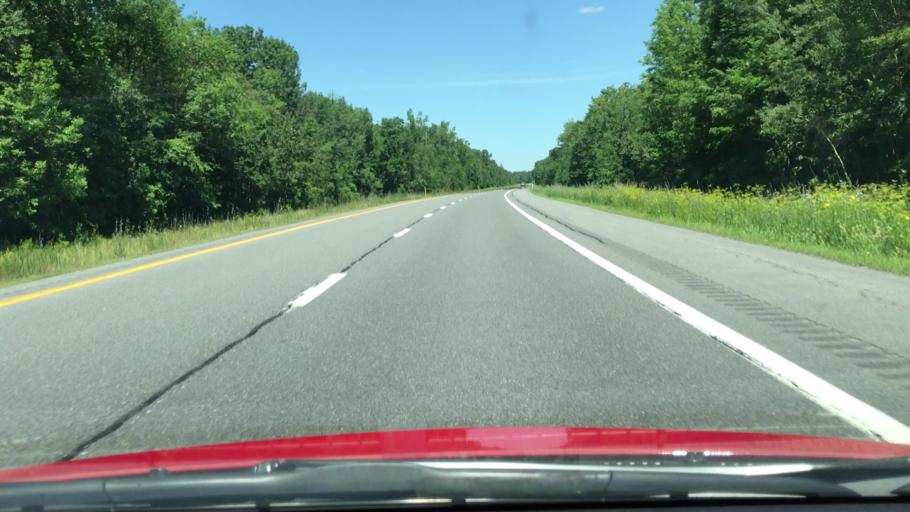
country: US
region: New York
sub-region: Clinton County
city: Champlain
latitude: 44.9025
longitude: -73.4536
